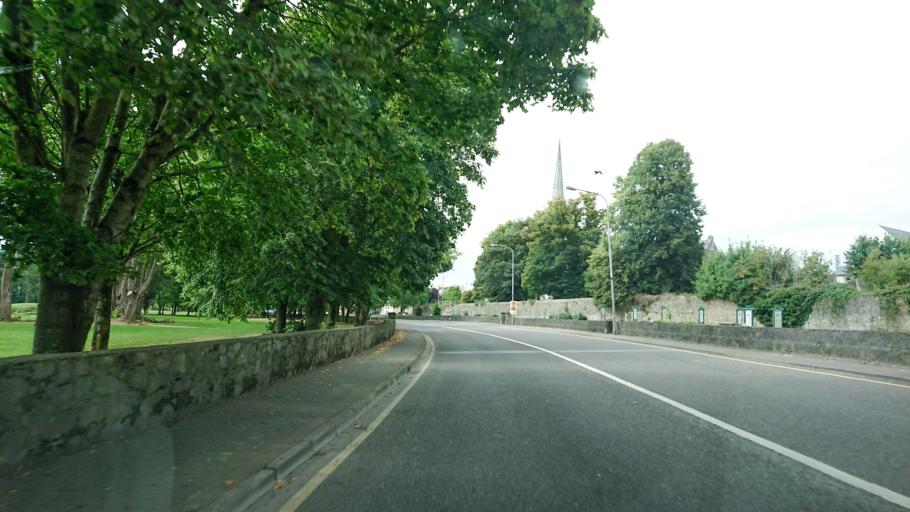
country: IE
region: Munster
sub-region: County Cork
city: Mallow
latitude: 52.1346
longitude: -8.6426
